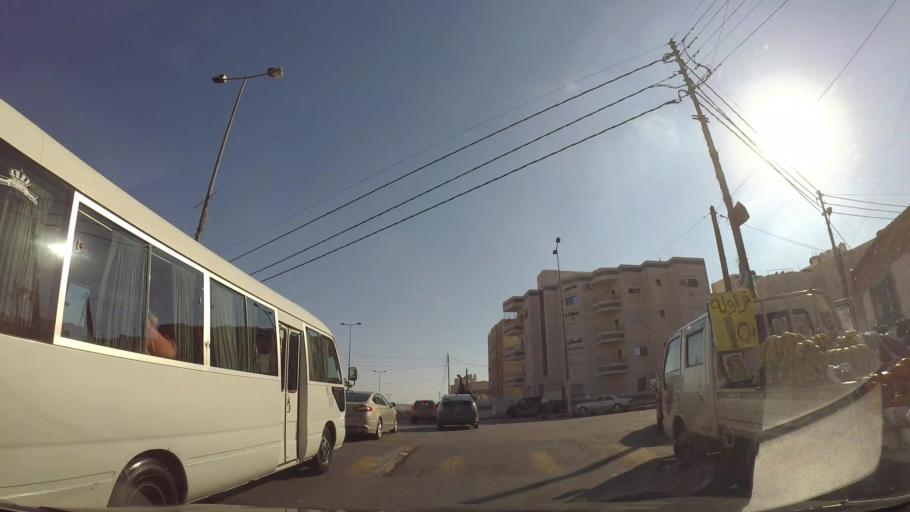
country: JO
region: Amman
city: Amman
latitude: 31.9737
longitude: 35.9386
